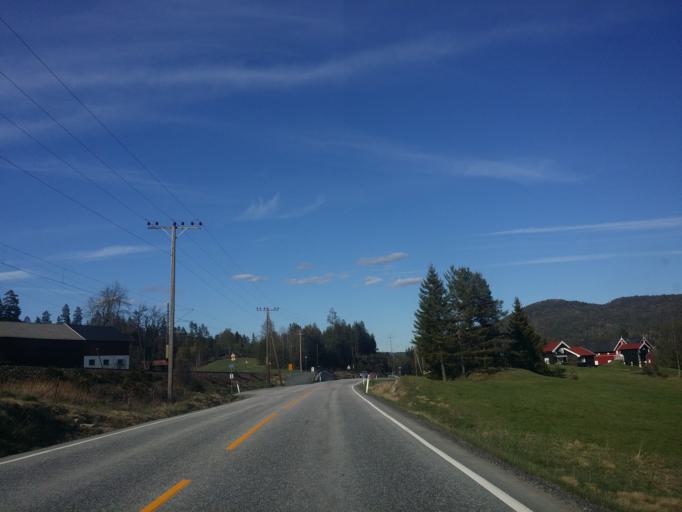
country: NO
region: Telemark
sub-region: Notodden
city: Notodden
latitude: 59.6100
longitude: 9.4502
